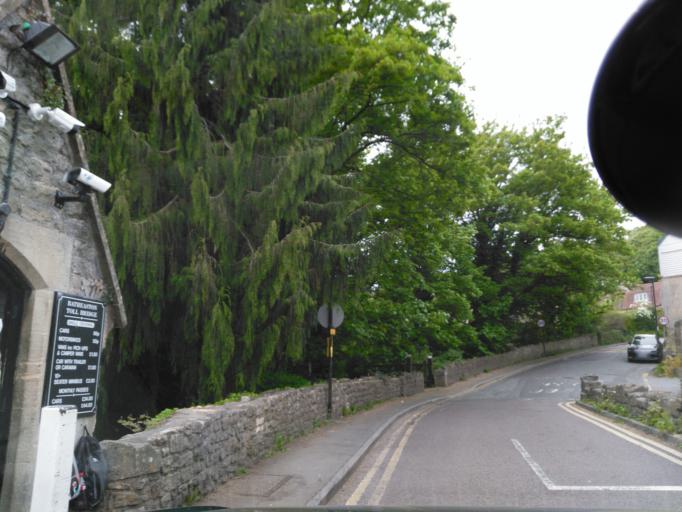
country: GB
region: England
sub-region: Bath and North East Somerset
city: Bath
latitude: 51.4018
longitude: -2.3260
